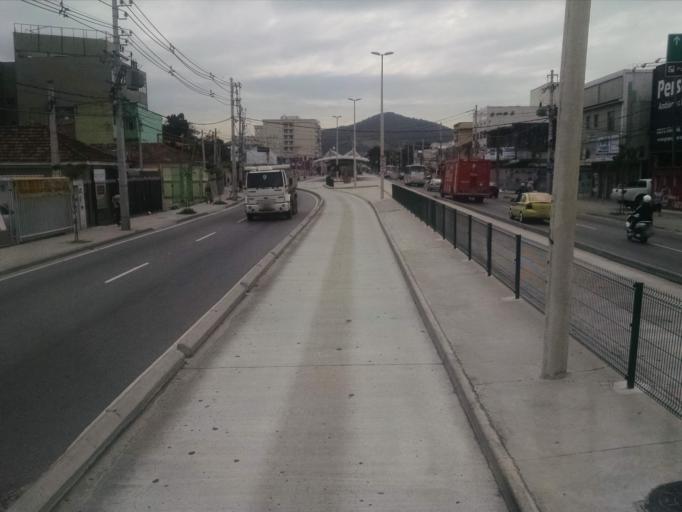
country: BR
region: Rio de Janeiro
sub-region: Sao Joao De Meriti
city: Sao Joao de Meriti
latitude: -22.9310
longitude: -43.3733
